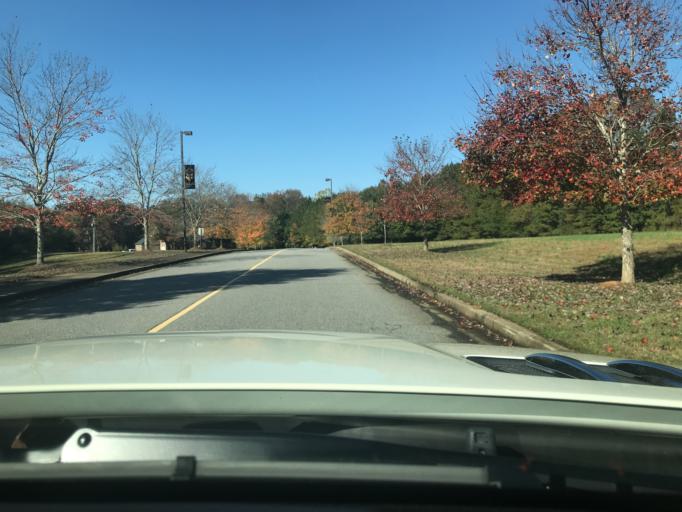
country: US
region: Georgia
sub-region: Gwinnett County
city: Duluth
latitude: 34.0435
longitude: -84.1280
